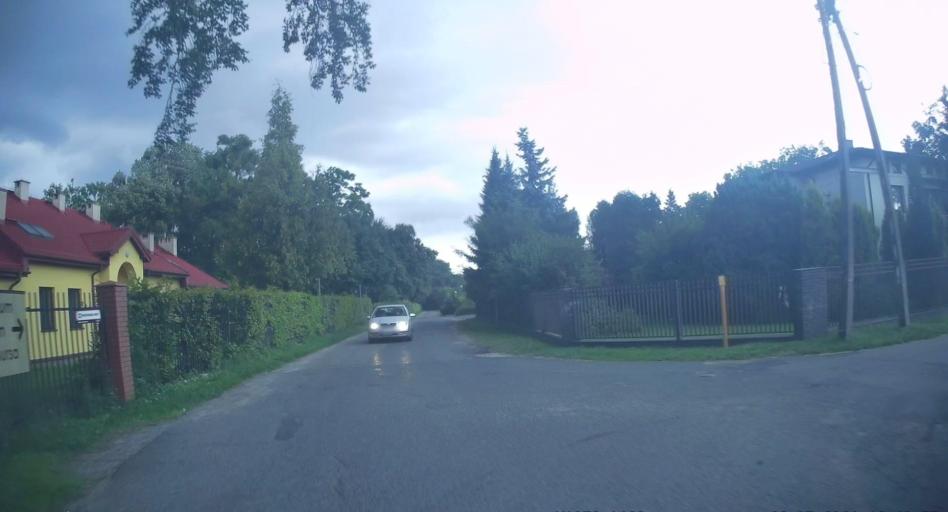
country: PL
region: Lodz Voivodeship
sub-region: Powiat brzezinski
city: Rogow
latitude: 51.8218
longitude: 19.8986
